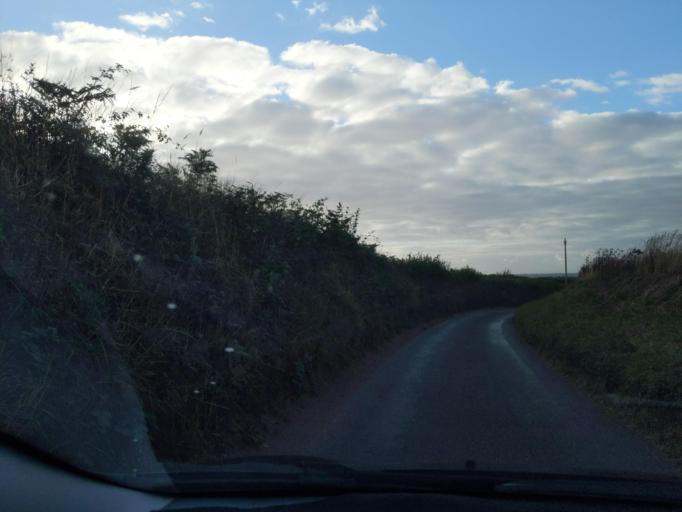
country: GB
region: England
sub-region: Devon
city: Salcombe
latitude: 50.2341
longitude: -3.8186
